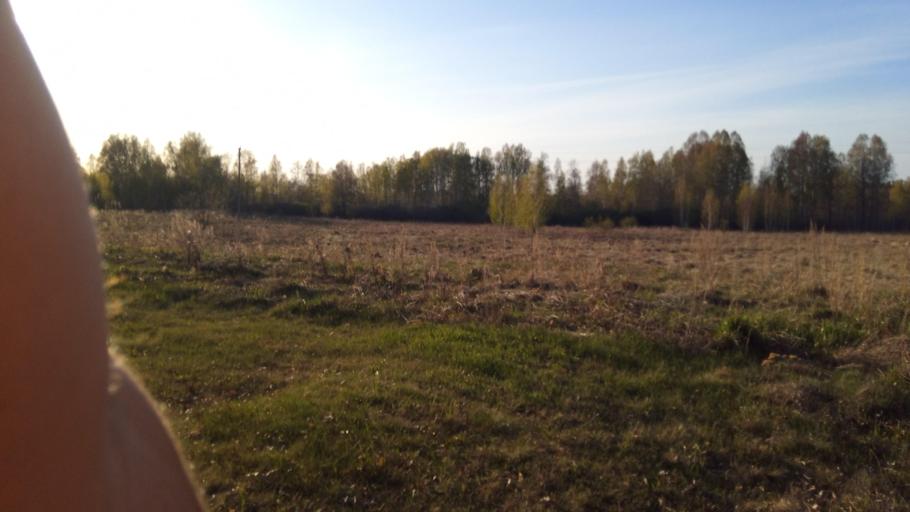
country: RU
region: Chelyabinsk
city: Timiryazevskiy
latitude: 54.9944
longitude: 60.8483
